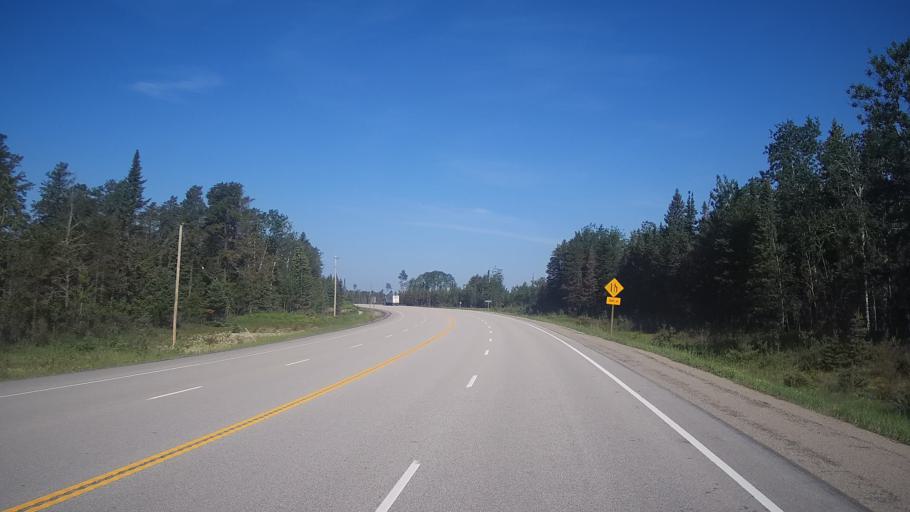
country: CA
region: Ontario
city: Dryden
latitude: 49.5648
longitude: -92.2278
